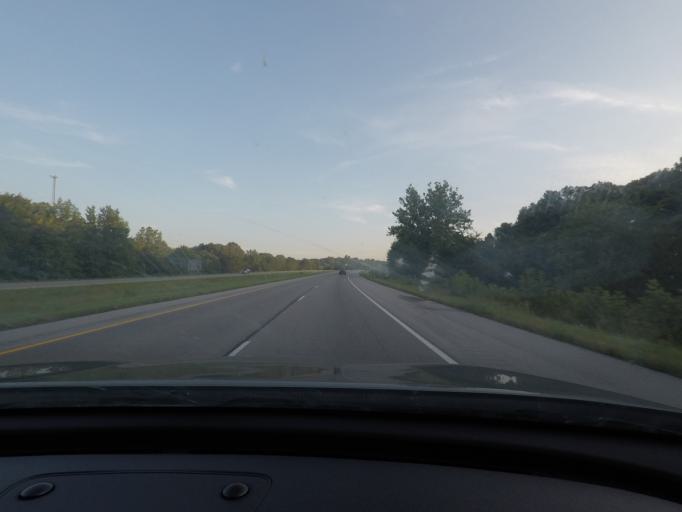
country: US
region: Illinois
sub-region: Johnson County
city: Vienna
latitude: 37.4337
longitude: -88.8820
